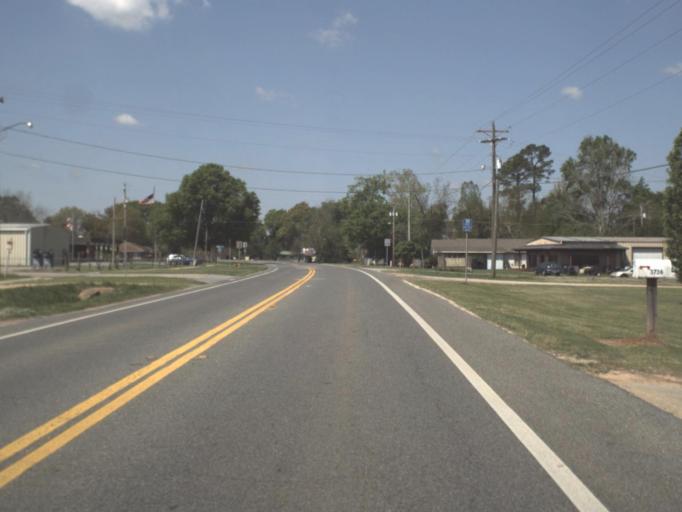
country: US
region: Florida
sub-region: Escambia County
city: Century
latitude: 30.9531
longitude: -87.1585
